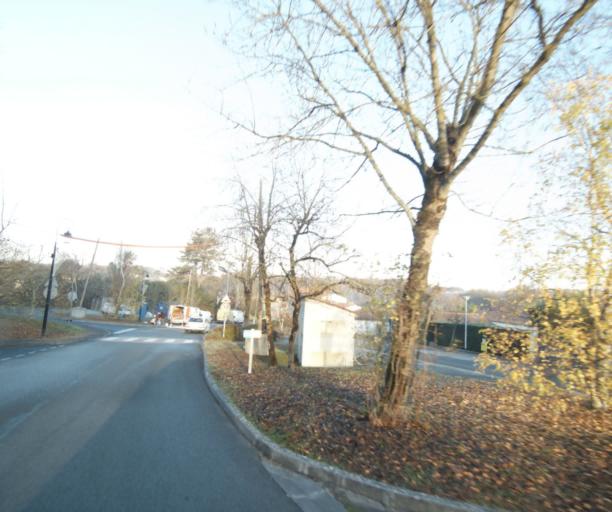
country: FR
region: Poitou-Charentes
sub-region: Departement de la Charente-Maritime
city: Fontcouverte
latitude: 45.7701
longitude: -0.5910
